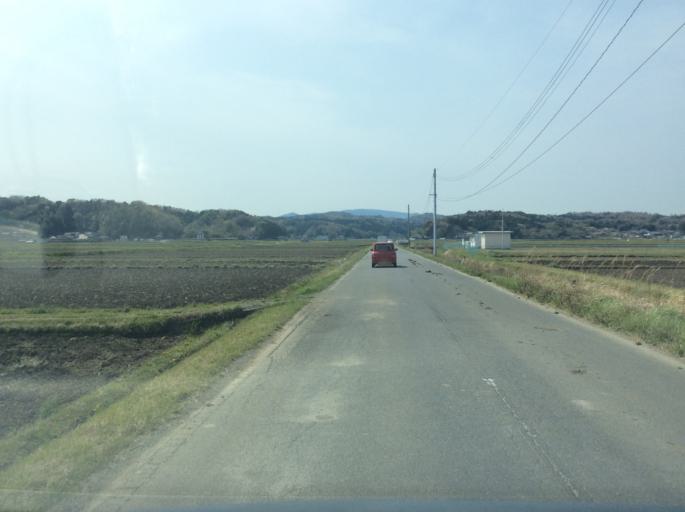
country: JP
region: Fukushima
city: Iwaki
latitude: 37.0890
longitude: 140.9526
